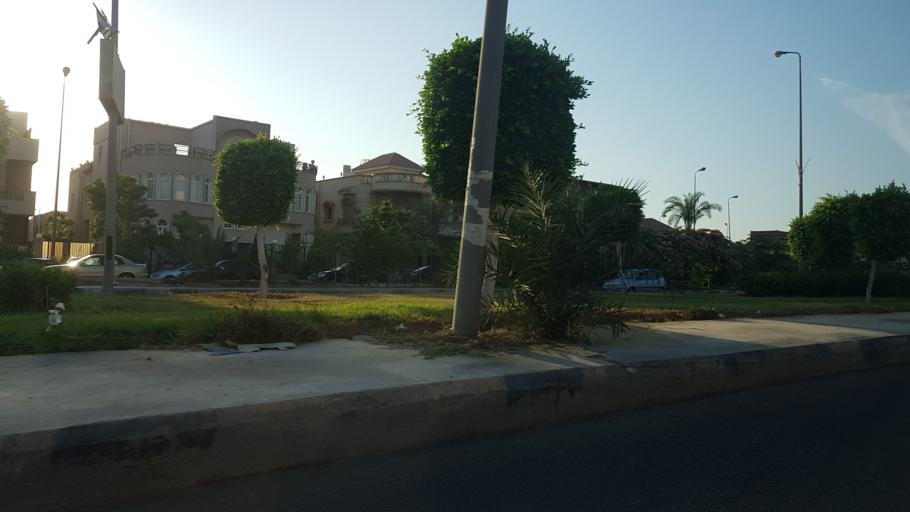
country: EG
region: Muhafazat al Qalyubiyah
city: Al Khankah
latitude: 30.0390
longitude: 31.4398
